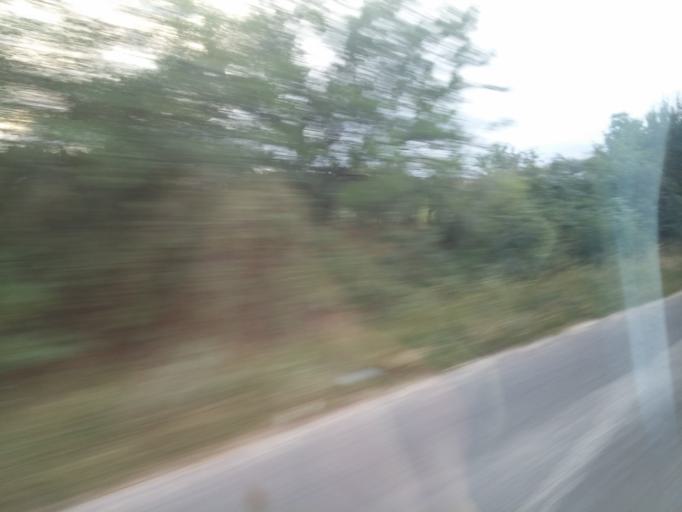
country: HU
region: Veszprem
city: Varpalota
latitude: 47.2161
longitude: 18.1510
